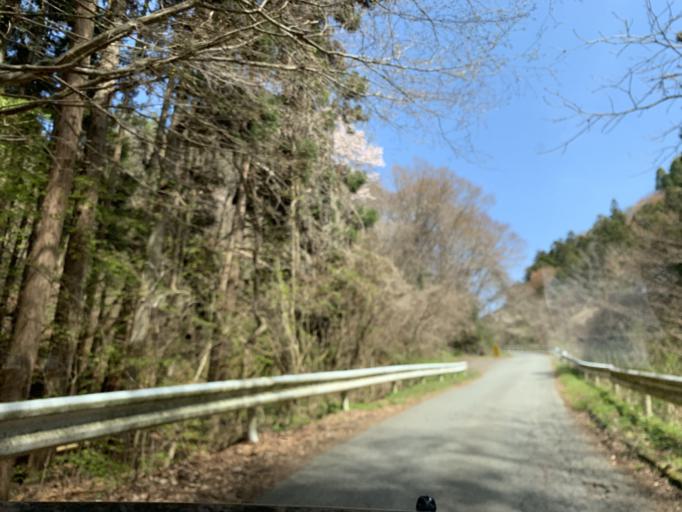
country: JP
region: Iwate
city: Ichinoseki
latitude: 38.7975
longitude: 141.2574
